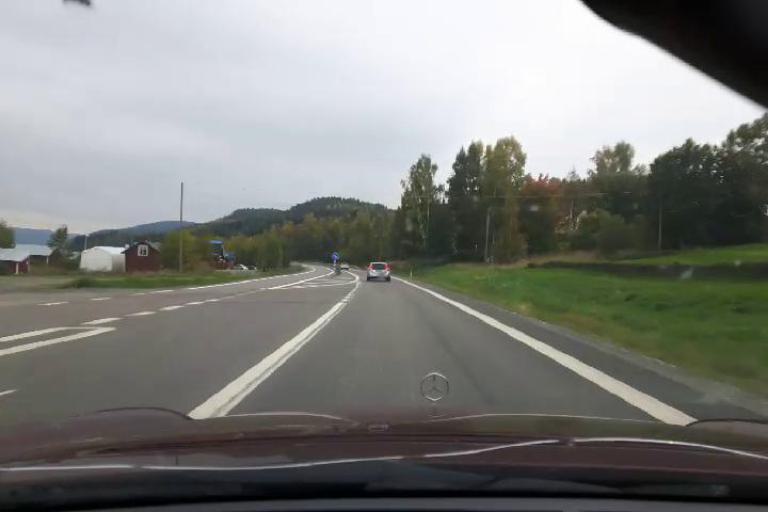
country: SE
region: Vaesternorrland
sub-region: Kramfors Kommun
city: Nordingra
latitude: 63.0482
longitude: 18.3258
